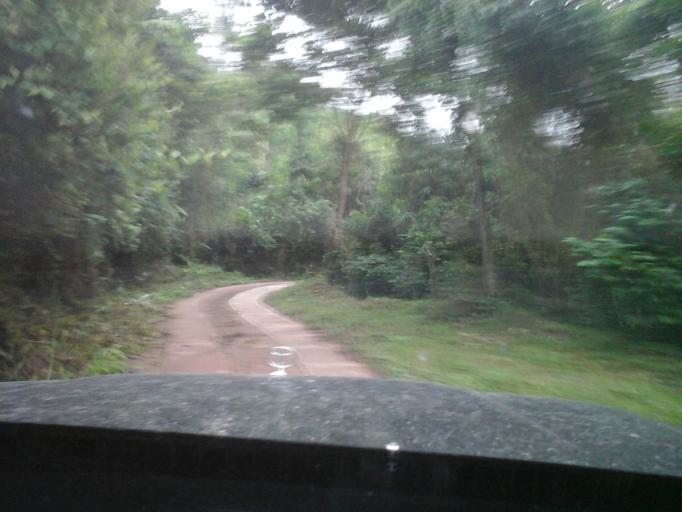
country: CO
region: Cesar
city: Agustin Codazzi
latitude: 9.9397
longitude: -73.1325
